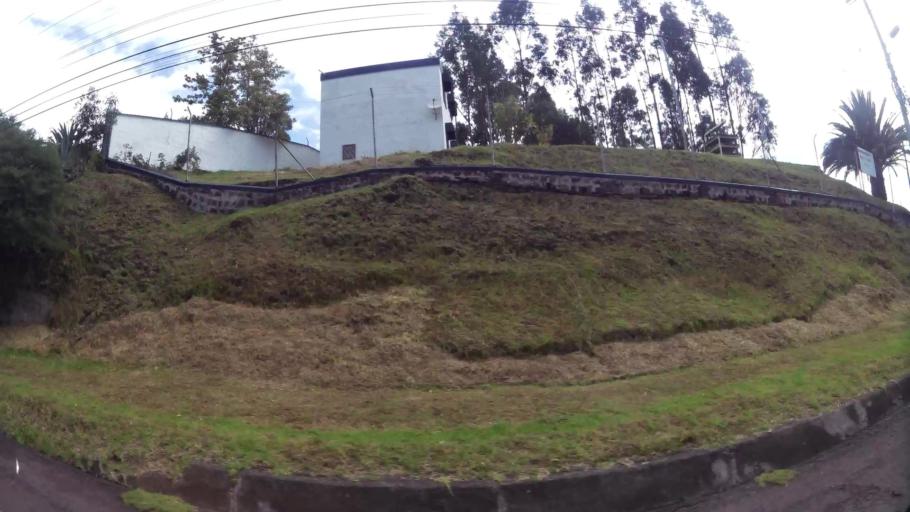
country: EC
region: Pichincha
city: Sangolqui
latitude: -0.3214
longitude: -78.3984
